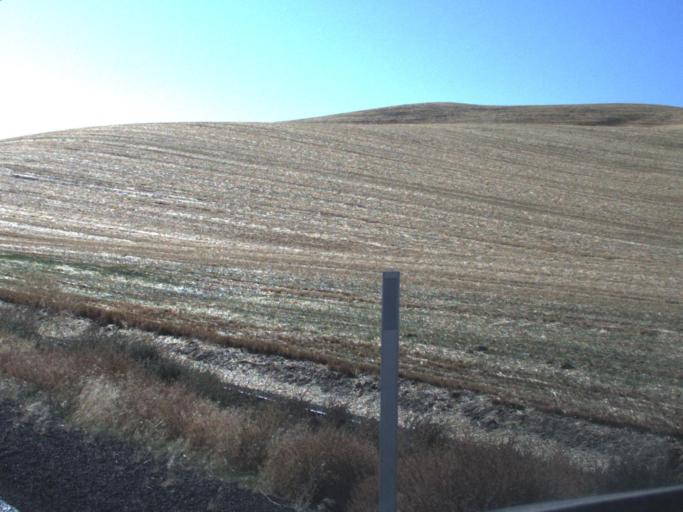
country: US
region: Washington
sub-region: Walla Walla County
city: Walla Walla
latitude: 46.2623
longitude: -118.3537
